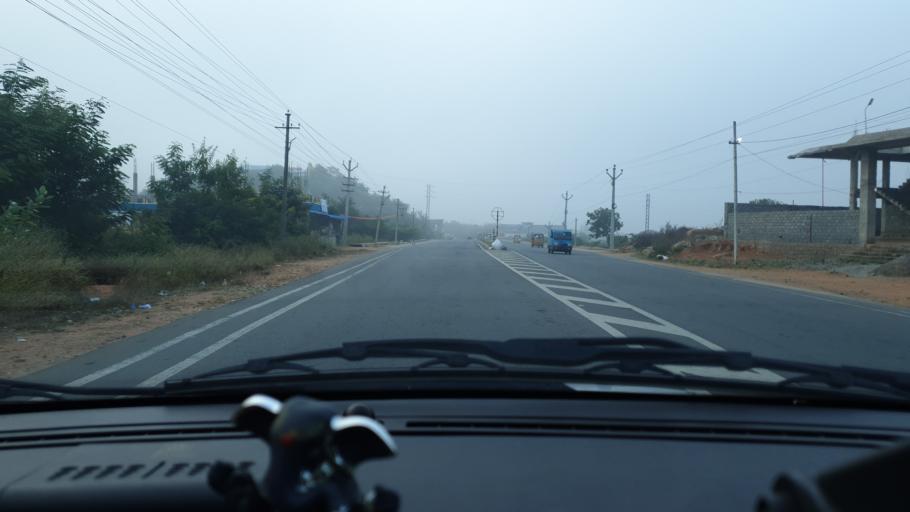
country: IN
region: Telangana
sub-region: Mahbubnagar
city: Farrukhnagar
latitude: 16.8639
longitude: 78.5287
